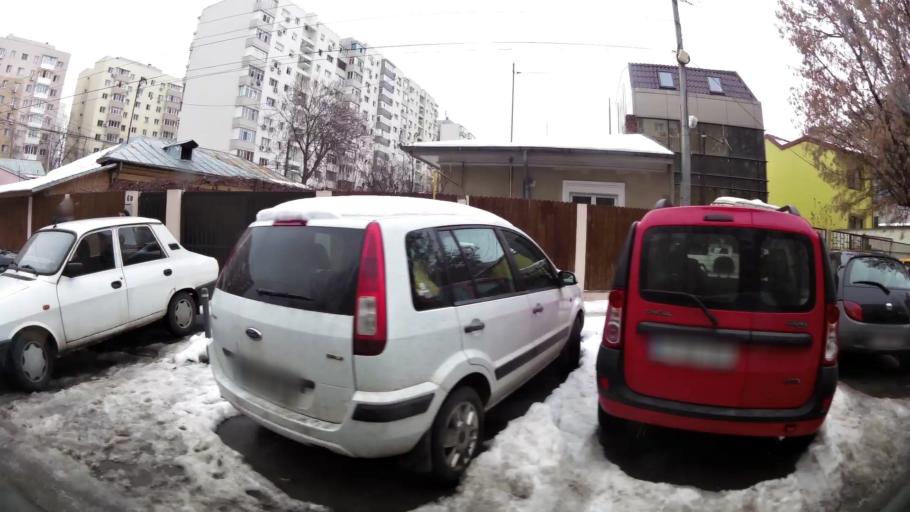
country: RO
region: Ilfov
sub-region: Comuna Popesti-Leordeni
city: Popesti-Leordeni
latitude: 44.4133
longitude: 26.1688
